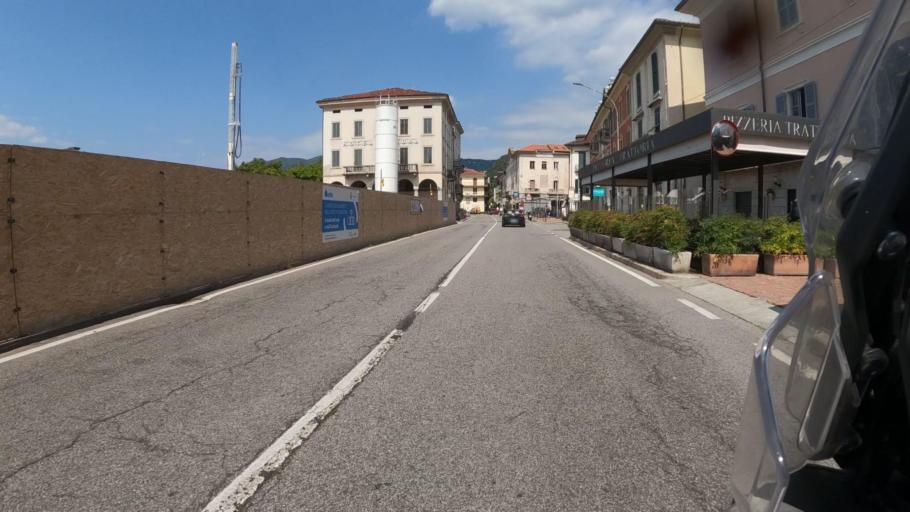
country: IT
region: Lombardy
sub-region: Provincia di Varese
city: Luino
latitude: 46.0028
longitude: 8.7424
